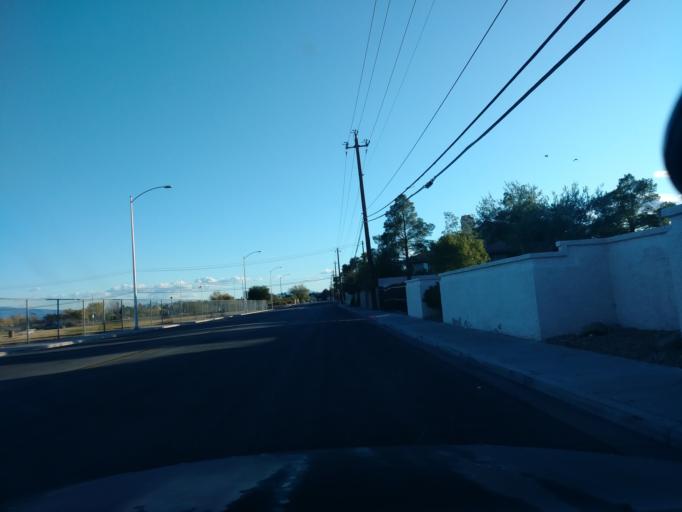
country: US
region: Nevada
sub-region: Clark County
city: Spring Valley
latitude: 36.1530
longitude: -115.2390
